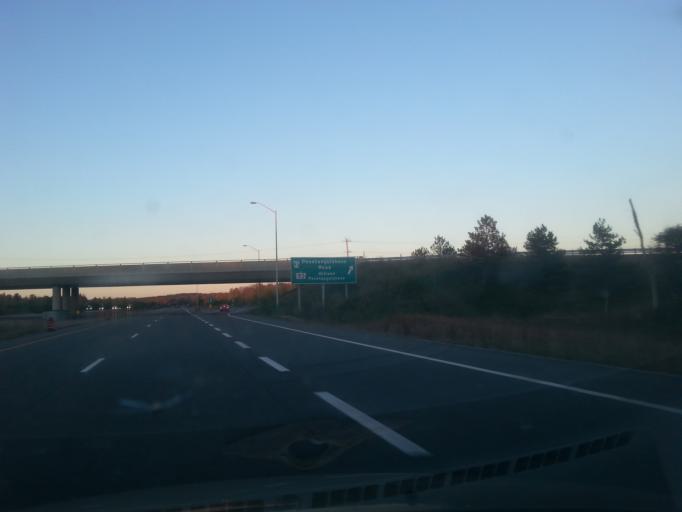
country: CA
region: Ontario
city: Barrie
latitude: 44.5514
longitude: -79.7460
